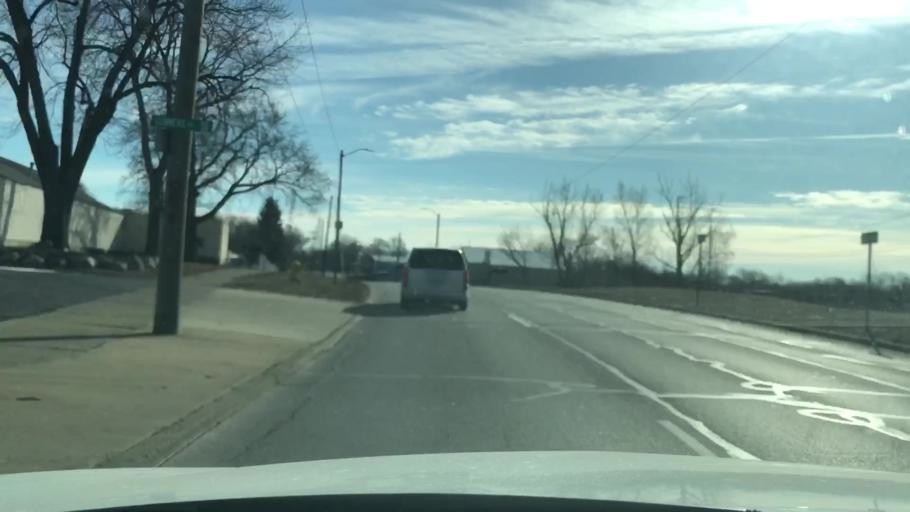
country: US
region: Michigan
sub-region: Oakland County
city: Pontiac
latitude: 42.6473
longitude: -83.3076
